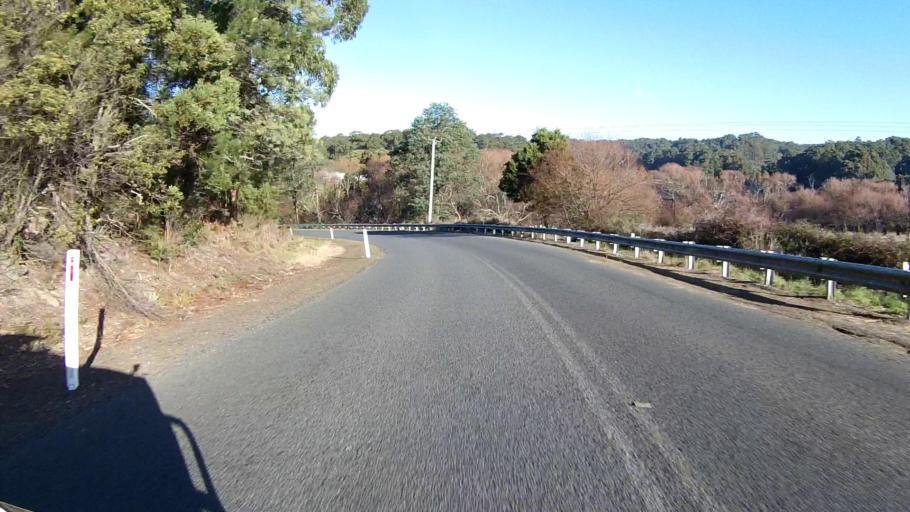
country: AU
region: Tasmania
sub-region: Clarence
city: Sandford
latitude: -43.1495
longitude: 147.8435
